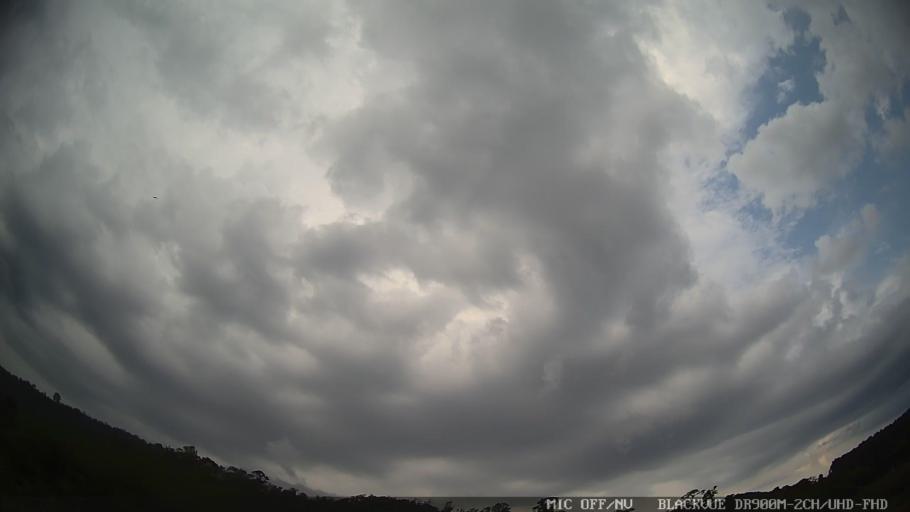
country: BR
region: Sao Paulo
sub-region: Itatiba
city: Itatiba
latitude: -23.0190
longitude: -46.8979
